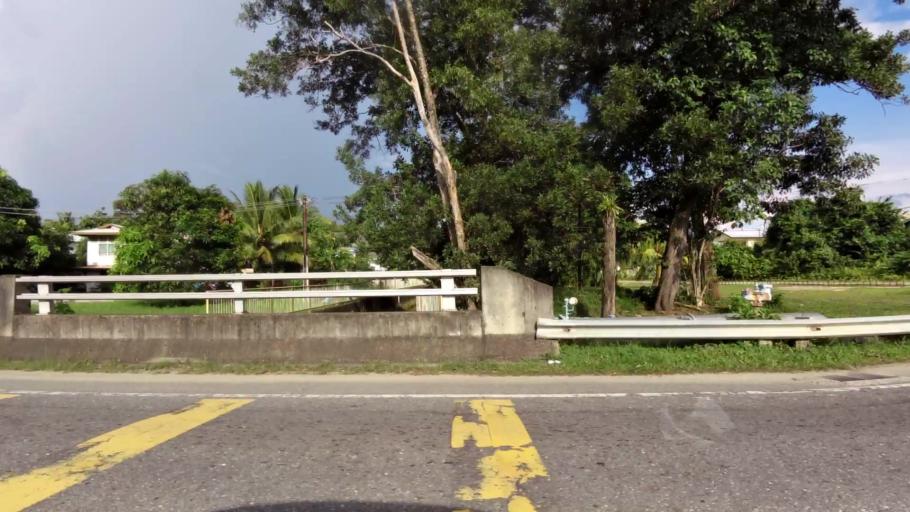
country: BN
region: Brunei and Muara
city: Bandar Seri Begawan
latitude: 4.9659
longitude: 114.9753
